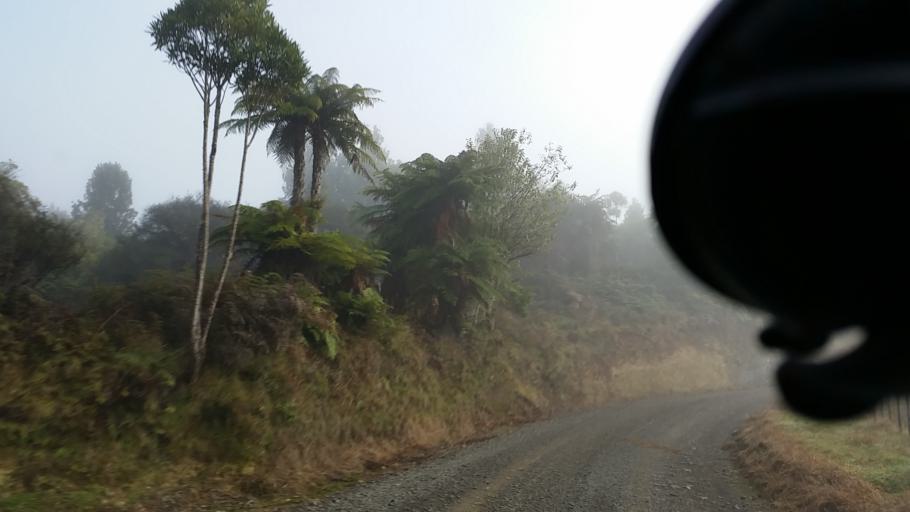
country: NZ
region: Taranaki
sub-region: New Plymouth District
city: Waitara
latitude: -38.9612
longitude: 174.7816
